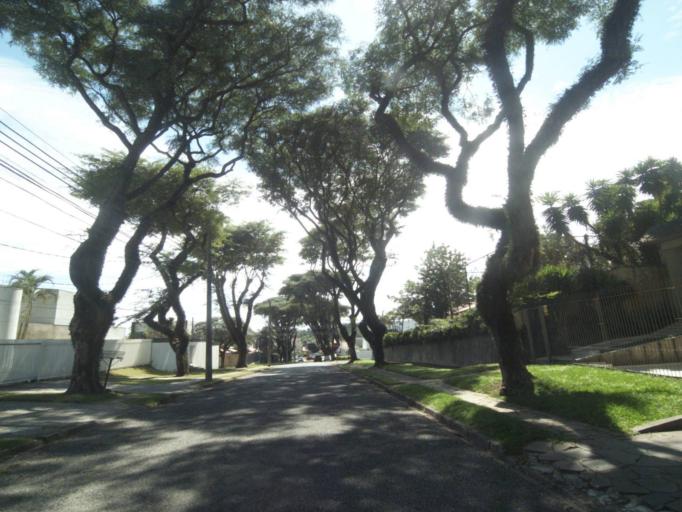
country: BR
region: Parana
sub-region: Curitiba
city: Curitiba
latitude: -25.4579
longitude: -49.2418
